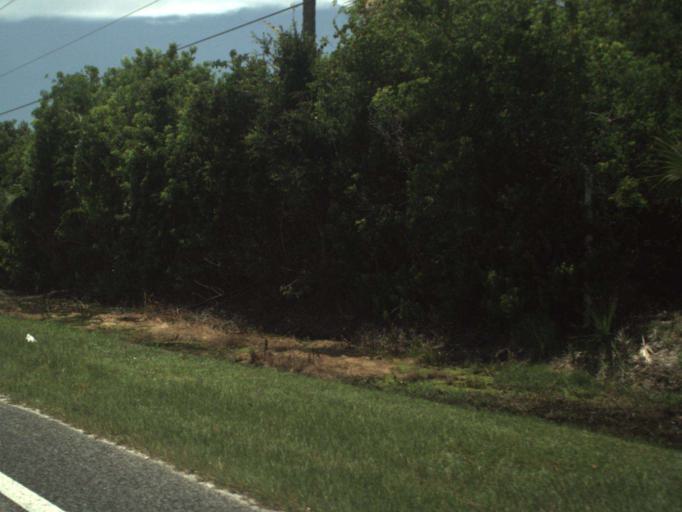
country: US
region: Florida
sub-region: Indian River County
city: Sebastian
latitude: 27.8045
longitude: -80.4642
